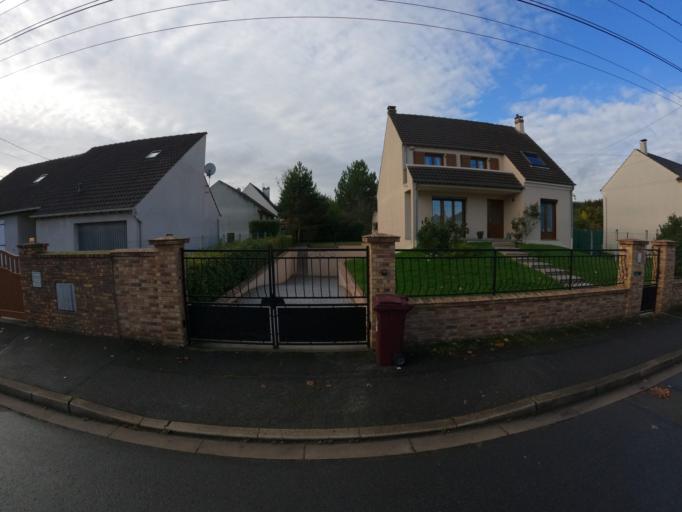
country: FR
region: Ile-de-France
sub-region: Departement de Seine-et-Marne
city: Le Pin
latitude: 48.8985
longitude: 2.6169
